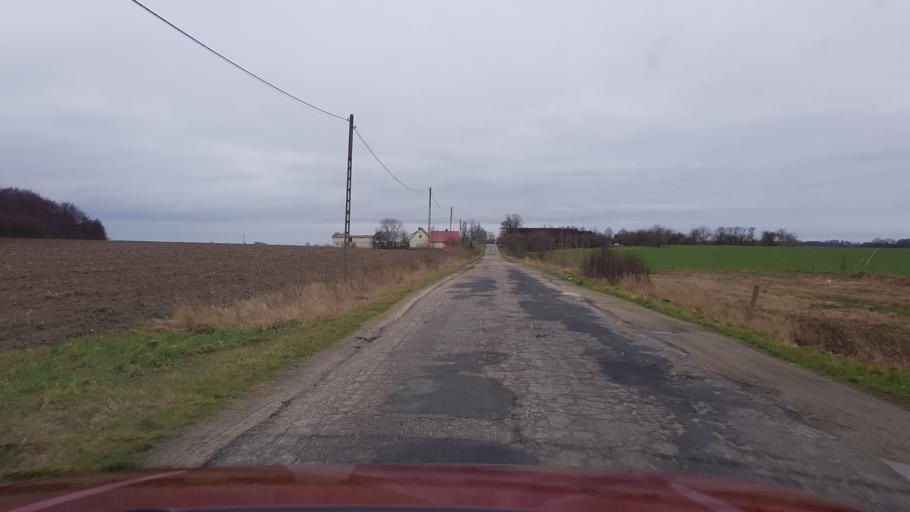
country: PL
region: West Pomeranian Voivodeship
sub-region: Powiat koszalinski
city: Mielno
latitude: 54.1852
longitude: 16.0194
